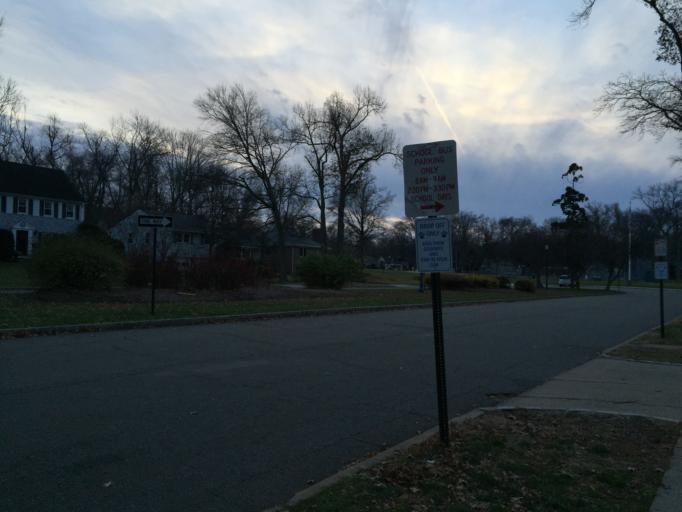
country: US
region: New Jersey
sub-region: Union County
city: Summit
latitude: 40.7079
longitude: -74.3643
